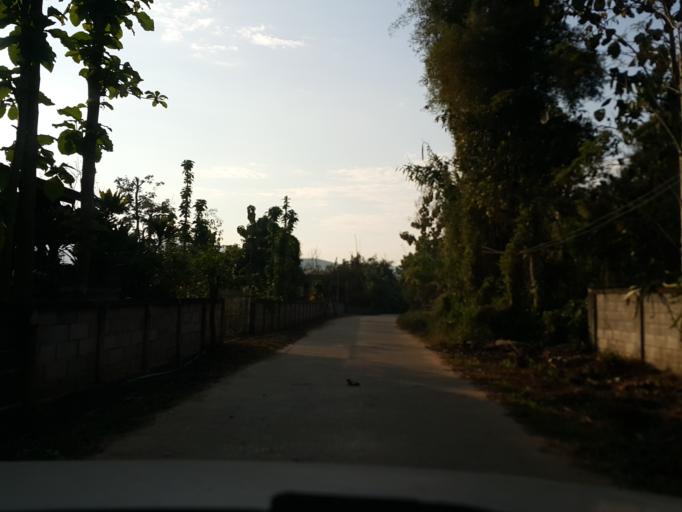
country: TH
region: Lamphun
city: Ban Thi
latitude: 18.5970
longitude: 99.2832
